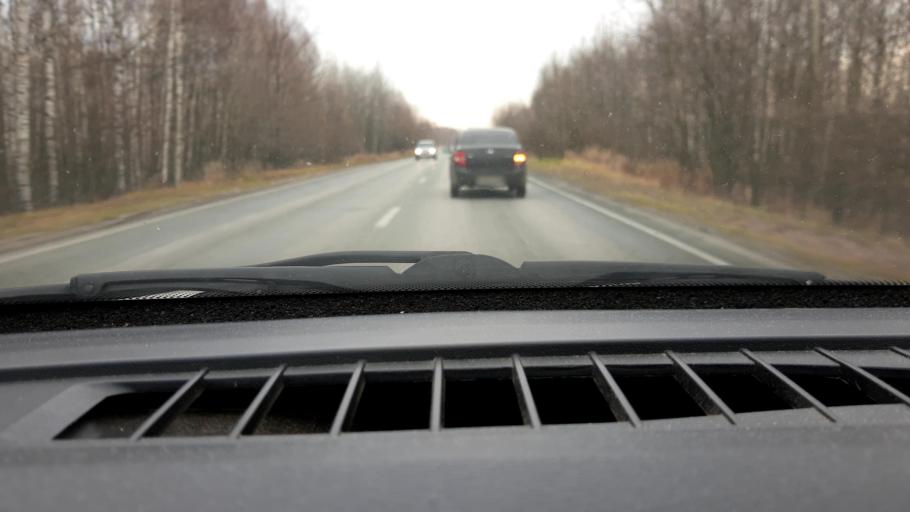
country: RU
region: Nizjnij Novgorod
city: Neklyudovo
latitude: 56.5262
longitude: 43.8328
